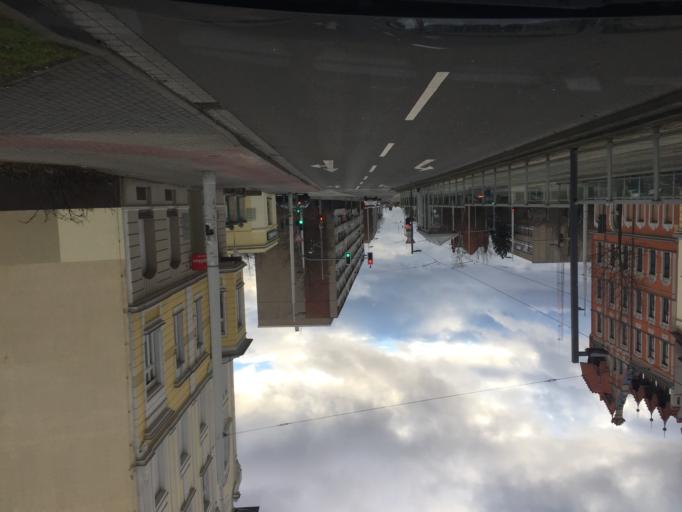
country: DE
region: Brandenburg
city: Cottbus
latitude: 51.7591
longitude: 14.3154
